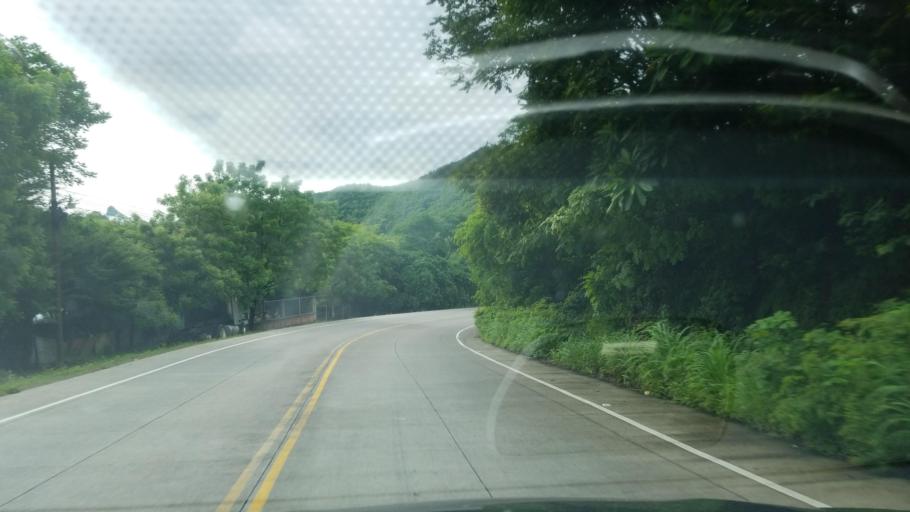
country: HN
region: Choluteca
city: Pespire
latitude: 13.6730
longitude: -87.3539
